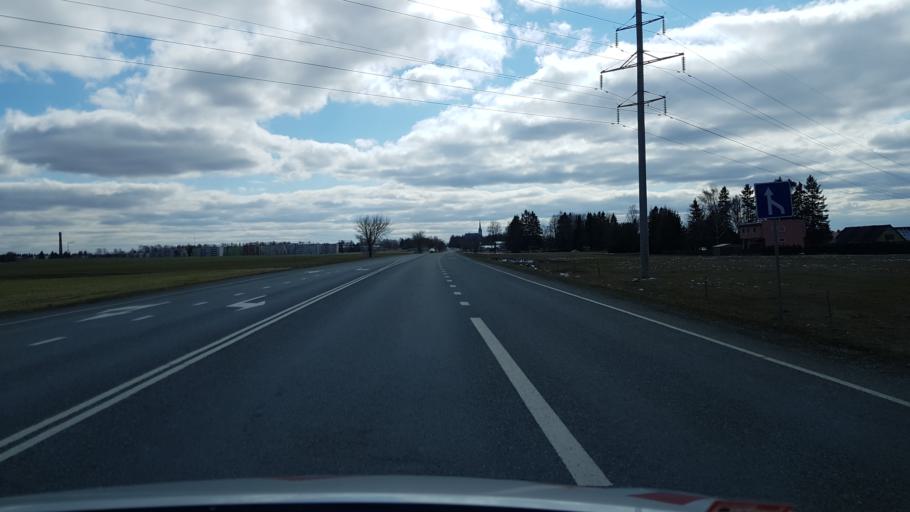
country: EE
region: Laeaene-Virumaa
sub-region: Kadrina vald
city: Kadrina
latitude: 59.3525
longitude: 26.1200
